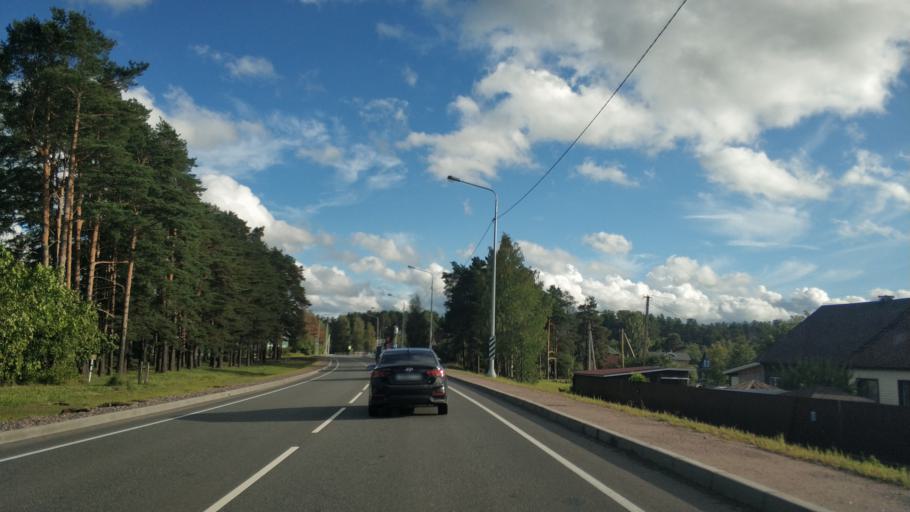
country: RU
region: Leningrad
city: Priozersk
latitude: 61.0011
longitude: 30.1816
